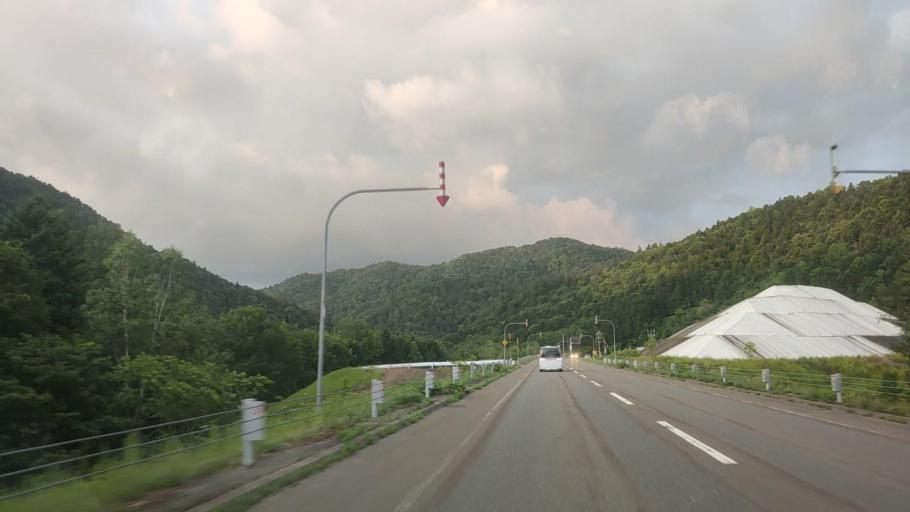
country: JP
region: Hokkaido
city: Ashibetsu
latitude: 43.3773
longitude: 142.2119
